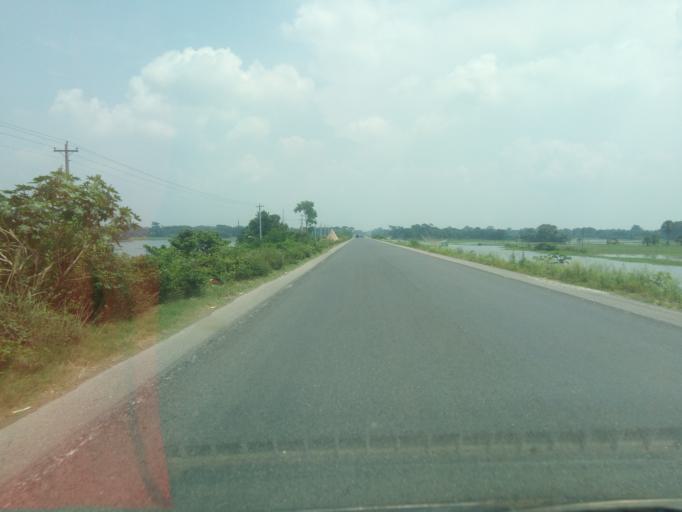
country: BD
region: Dhaka
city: Char Bhadrasan
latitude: 23.3785
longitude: 90.0120
